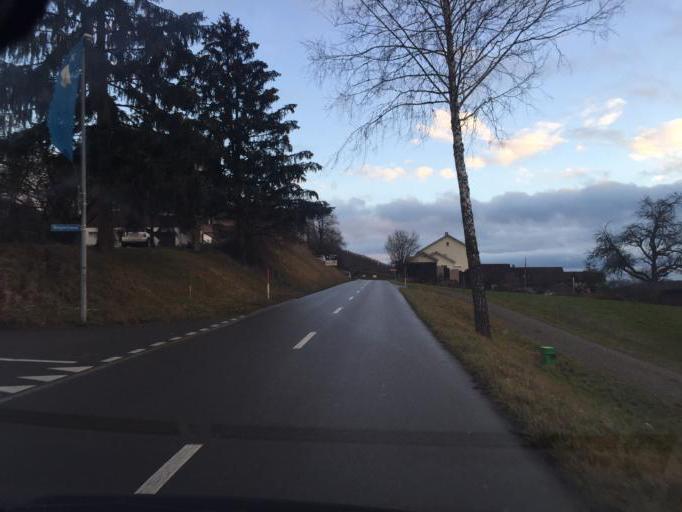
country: DE
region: Baden-Wuerttemberg
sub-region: Freiburg Region
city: Busingen
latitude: 47.7090
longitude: 8.7181
